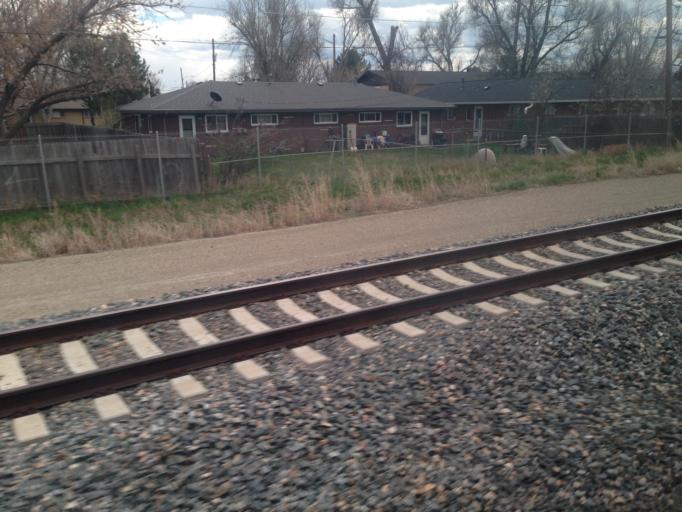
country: US
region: Colorado
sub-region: Jefferson County
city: Arvada
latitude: 39.7950
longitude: -105.0965
